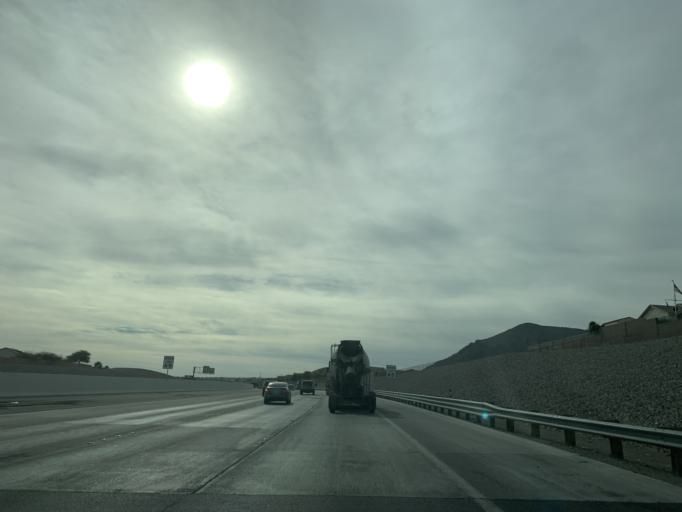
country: US
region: Nevada
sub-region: Clark County
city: Summerlin South
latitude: 36.2393
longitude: -115.3250
